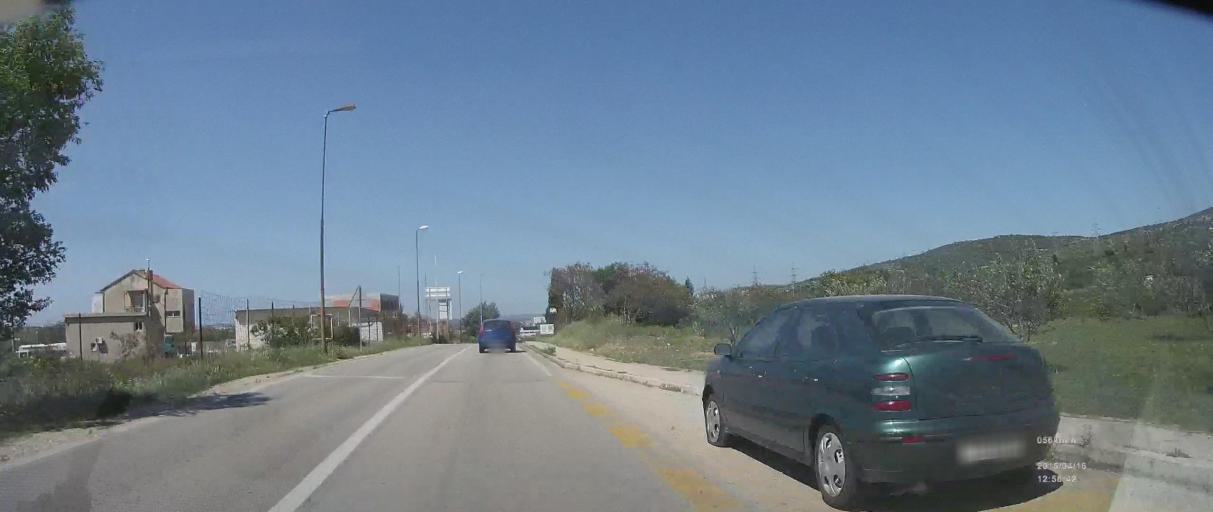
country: HR
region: Sibensko-Kniniska
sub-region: Grad Sibenik
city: Sibenik
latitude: 43.7104
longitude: 15.9206
